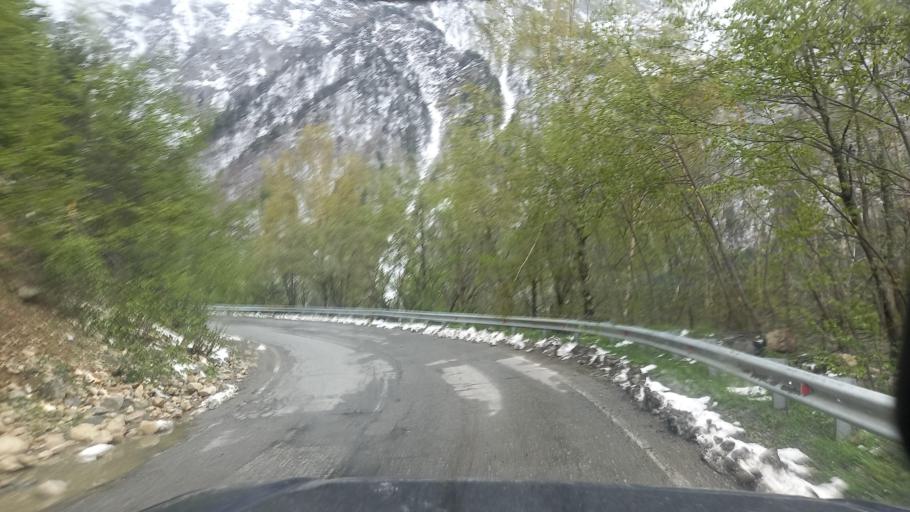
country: RU
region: North Ossetia
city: Mizur
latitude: 42.7999
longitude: 43.9350
